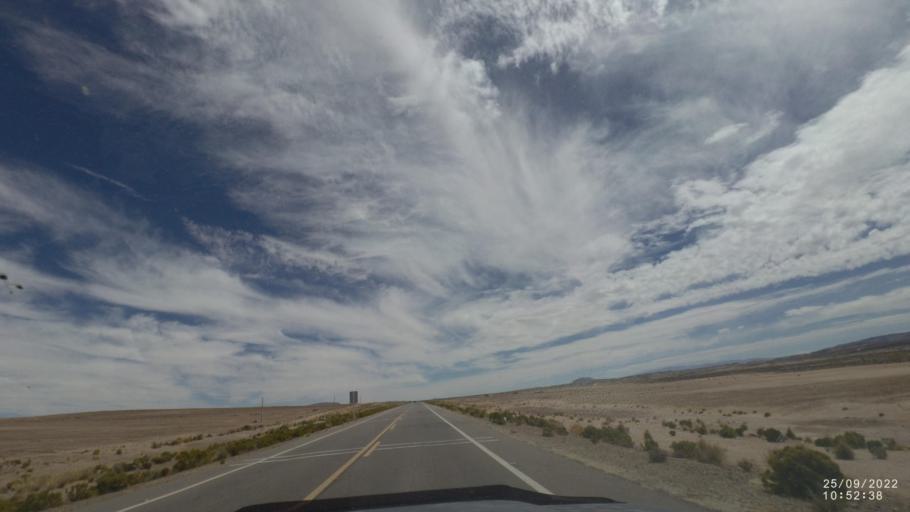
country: BO
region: Oruro
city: Challapata
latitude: -19.5453
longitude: -66.8540
